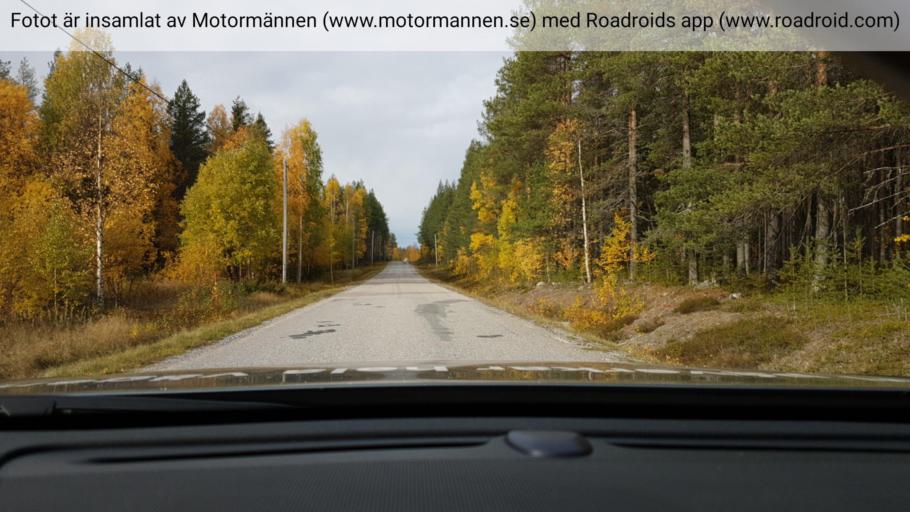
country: SE
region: Norrbotten
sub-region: Overkalix Kommun
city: OEverkalix
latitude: 66.2500
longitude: 23.1327
